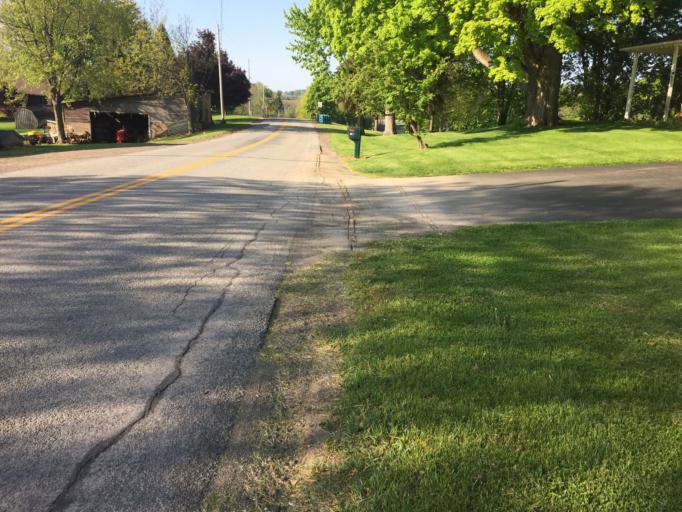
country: US
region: New York
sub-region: Wayne County
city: Marion
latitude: 43.1377
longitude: -77.1718
